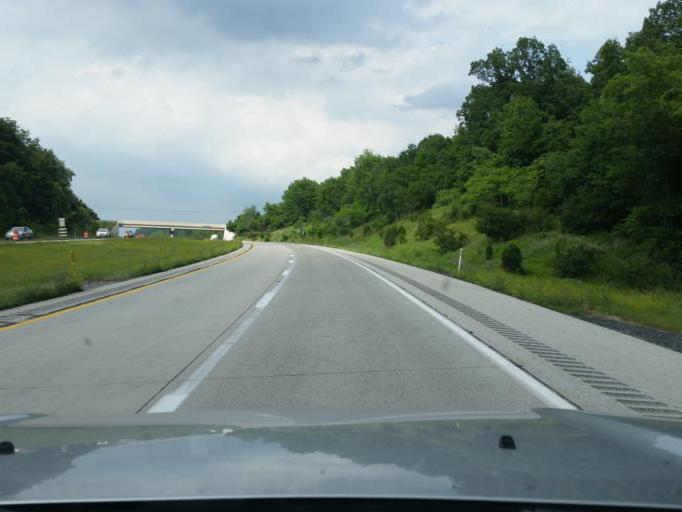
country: US
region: Maryland
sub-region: Frederick County
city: Emmitsburg
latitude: 39.7450
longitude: -77.2760
